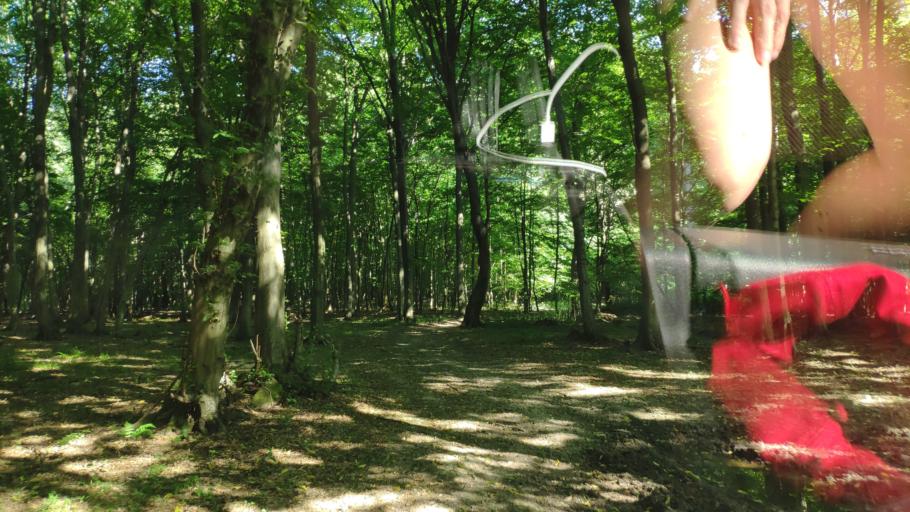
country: SK
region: Presovsky
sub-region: Okres Presov
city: Presov
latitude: 48.9063
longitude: 21.2911
